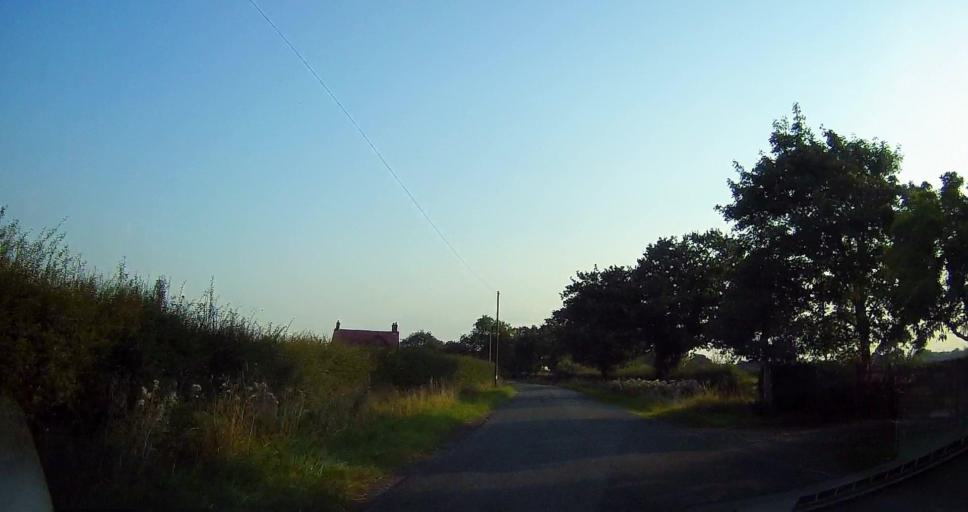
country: GB
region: England
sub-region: Cheshire East
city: Nantwich
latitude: 53.0166
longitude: -2.5228
